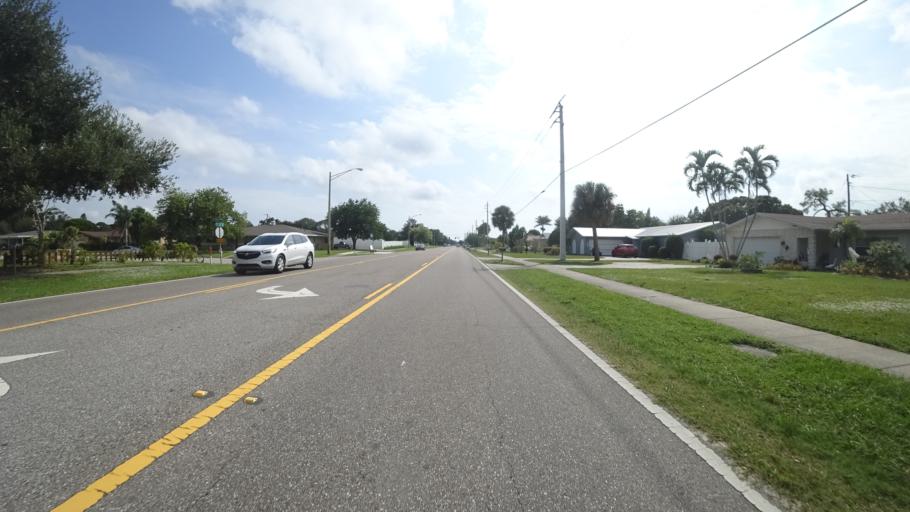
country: US
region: Florida
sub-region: Manatee County
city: West Bradenton
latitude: 27.4922
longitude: -82.6205
